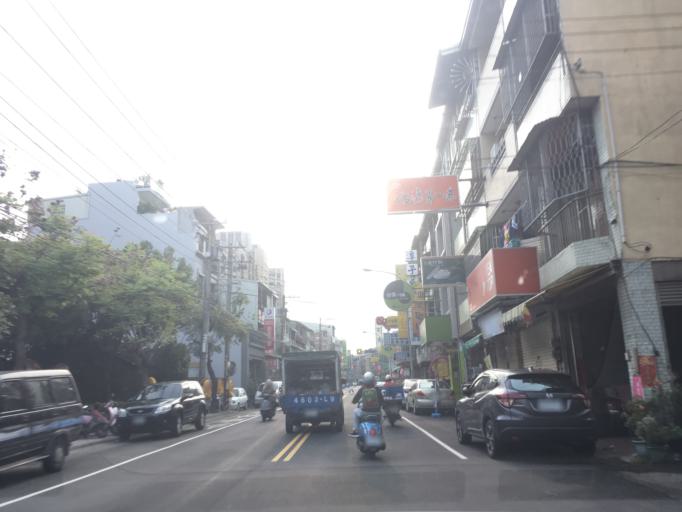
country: TW
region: Taiwan
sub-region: Taichung City
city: Taichung
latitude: 24.1946
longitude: 120.6980
